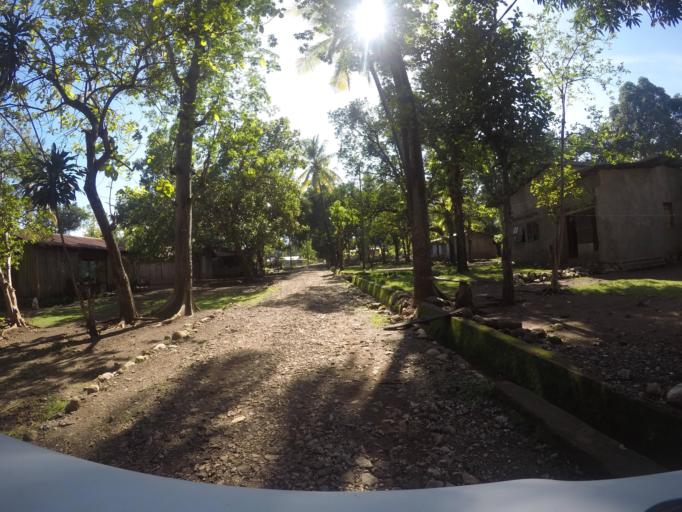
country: TL
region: Bobonaro
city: Maliana
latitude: -8.9911
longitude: 125.2033
